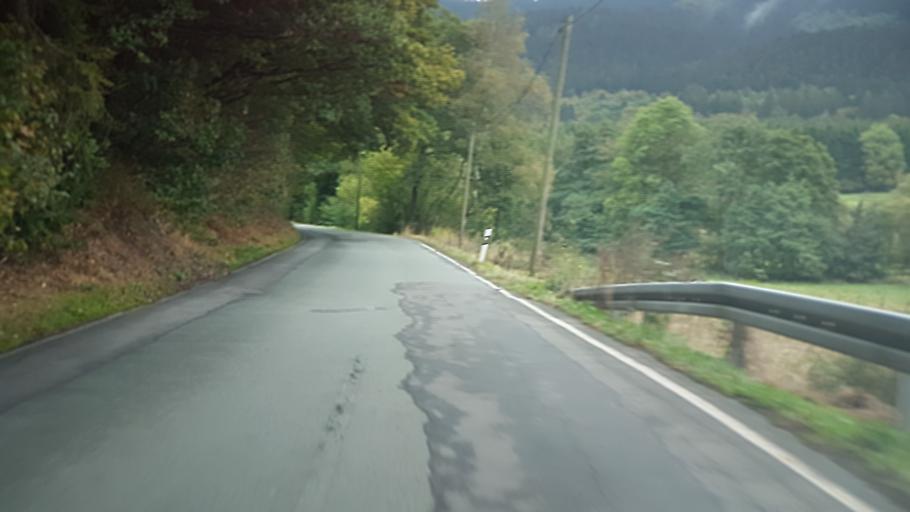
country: DE
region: North Rhine-Westphalia
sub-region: Regierungsbezirk Arnsberg
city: Herscheid
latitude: 51.1598
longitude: 7.7761
